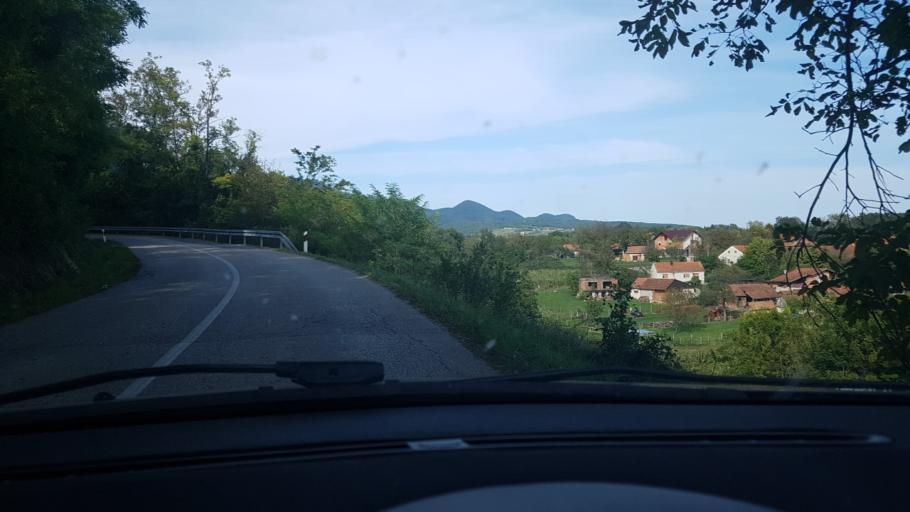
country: HR
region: Krapinsko-Zagorska
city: Zlatar
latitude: 46.1197
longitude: 16.1090
